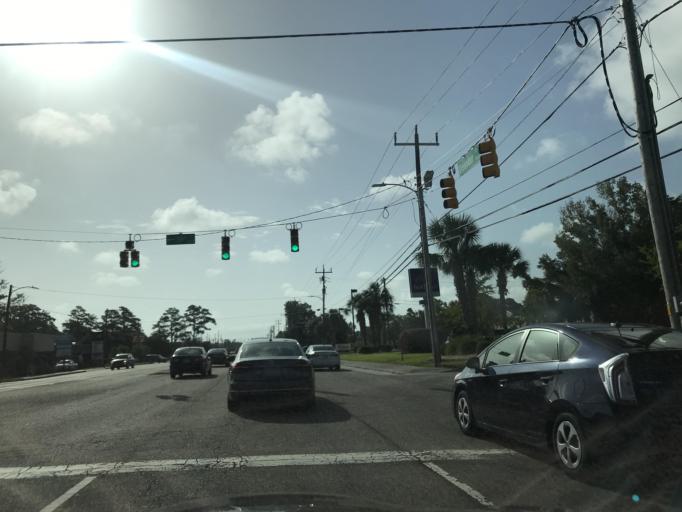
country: US
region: North Carolina
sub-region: New Hanover County
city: Wilmington
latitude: 34.2138
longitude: -77.8997
